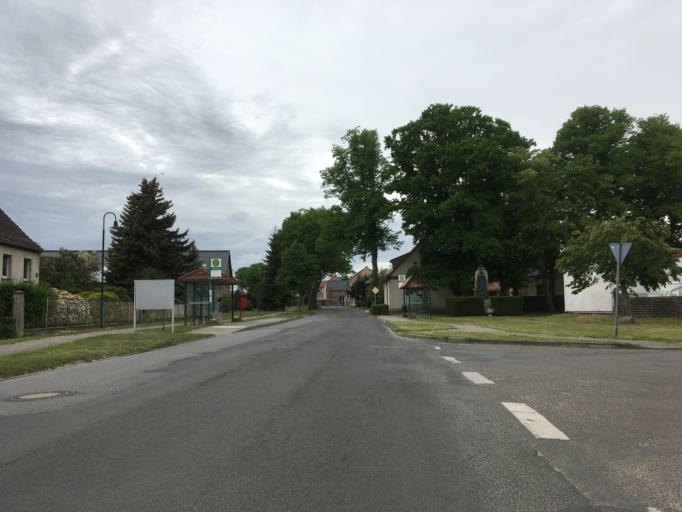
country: DE
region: Brandenburg
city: Werneuchen
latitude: 52.6636
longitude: 13.6831
